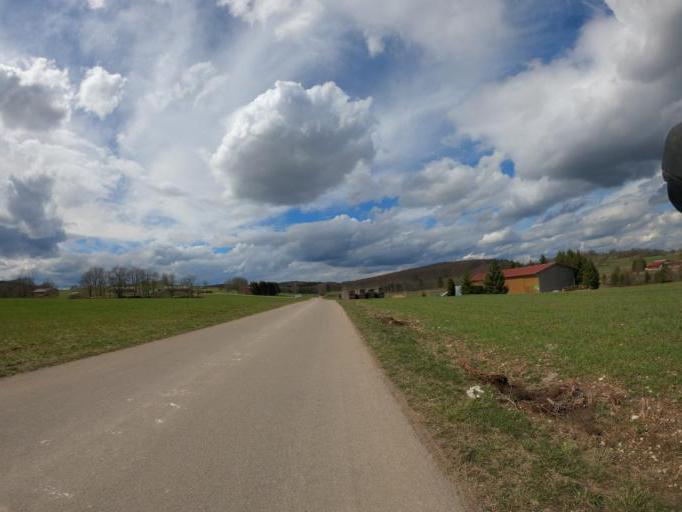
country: DE
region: Baden-Wuerttemberg
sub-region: Tuebingen Region
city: Pfullingen
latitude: 48.3971
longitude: 9.1734
